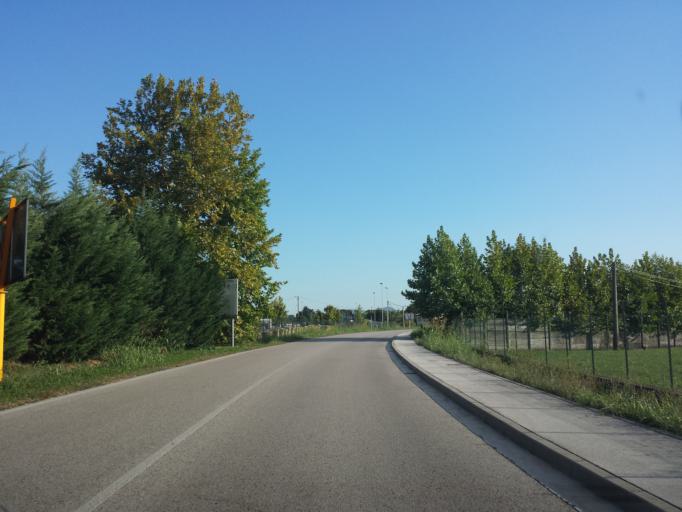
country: IT
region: Veneto
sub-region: Provincia di Vicenza
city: Torri di Quartesolo
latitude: 45.5210
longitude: 11.5971
